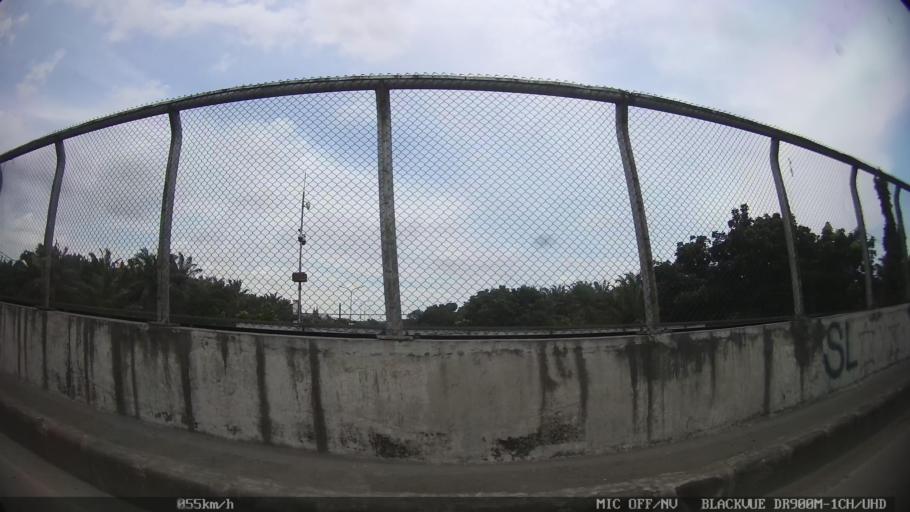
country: ID
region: North Sumatra
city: Labuhan Deli
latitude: 3.6732
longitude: 98.6811
